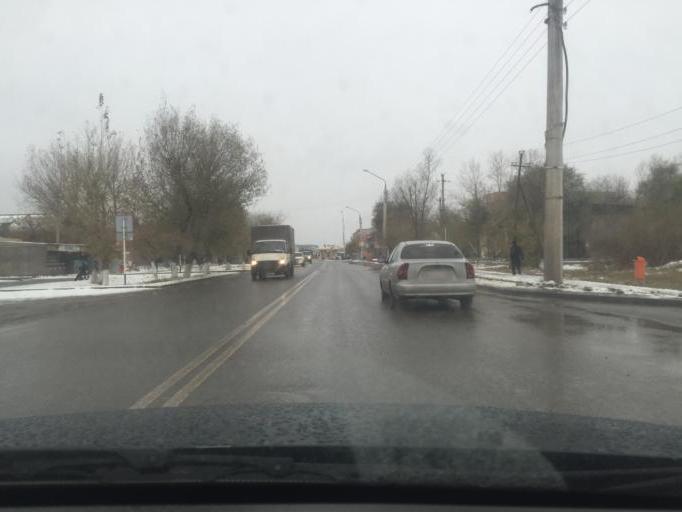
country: KZ
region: Astana Qalasy
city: Astana
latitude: 51.1994
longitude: 71.3904
